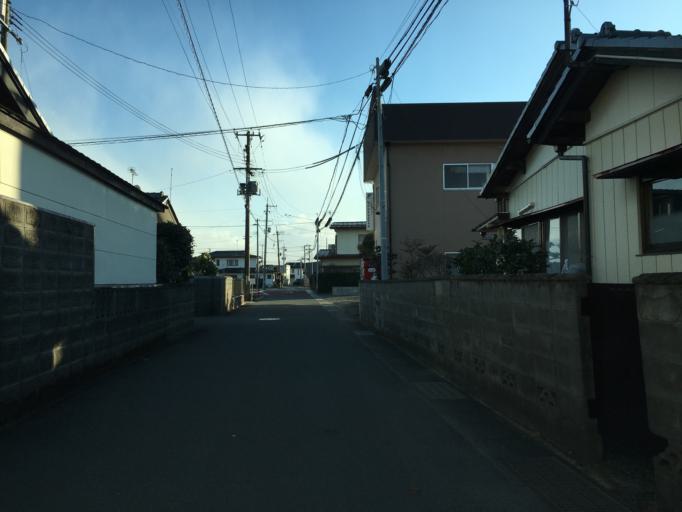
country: JP
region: Fukushima
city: Fukushima-shi
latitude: 37.7708
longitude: 140.4296
